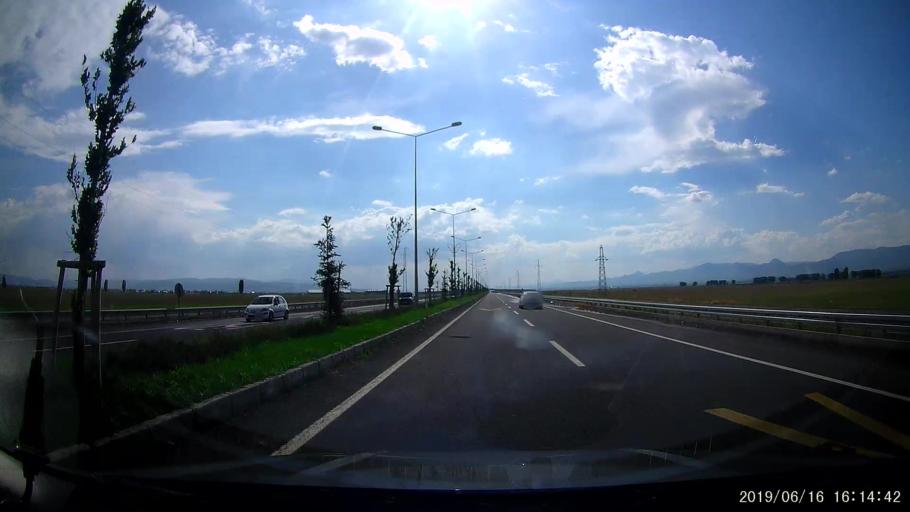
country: TR
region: Erzurum
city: Erzurum
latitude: 39.9611
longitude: 41.2423
